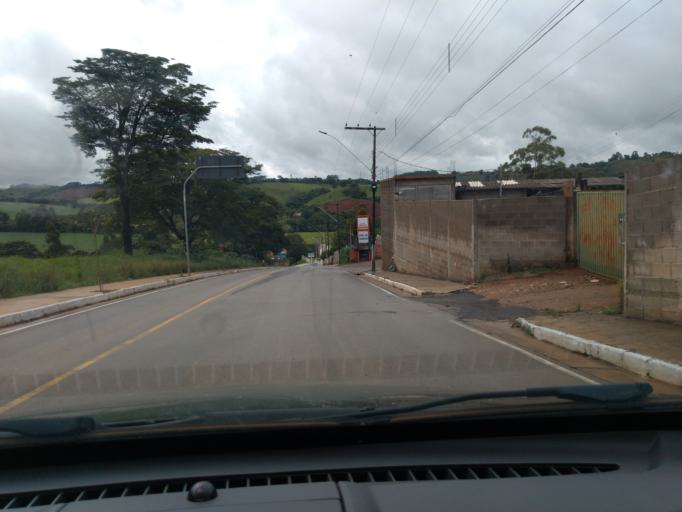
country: BR
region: Minas Gerais
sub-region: Lavras
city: Lavras
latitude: -21.5072
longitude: -44.9128
